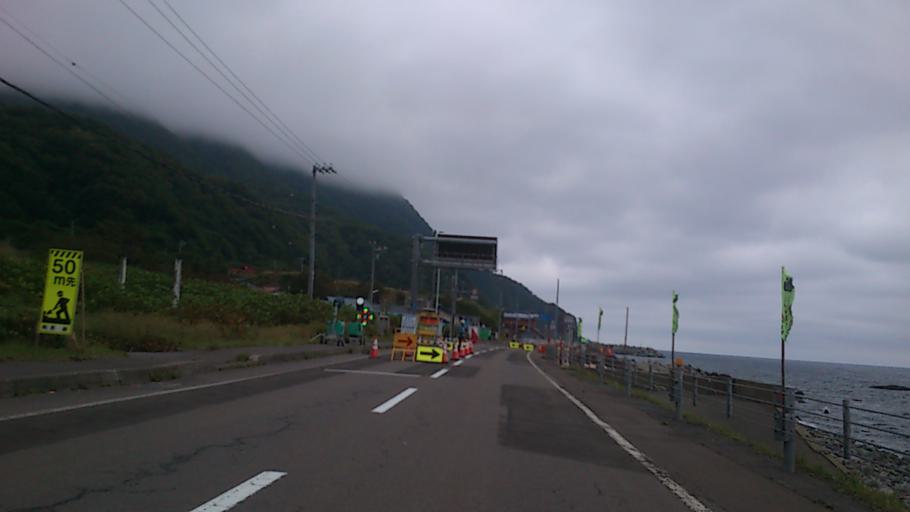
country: JP
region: Hokkaido
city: Iwanai
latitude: 42.6758
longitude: 139.8919
